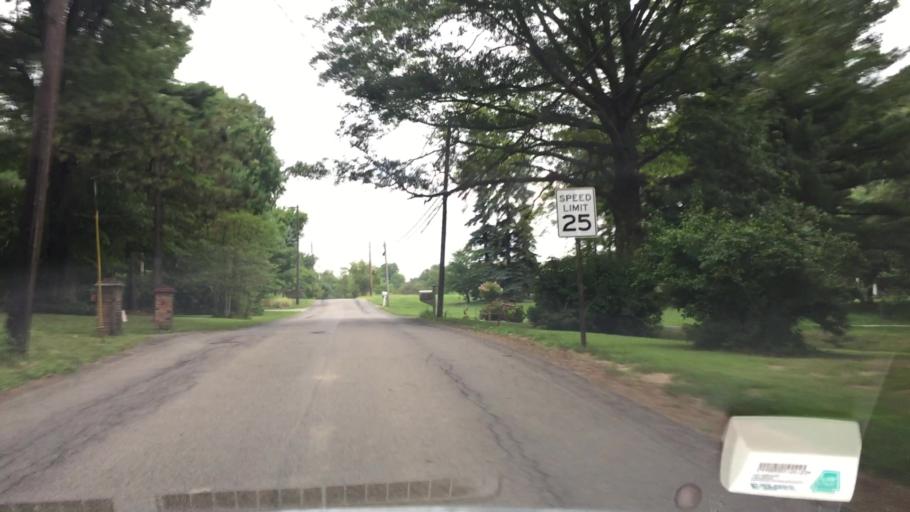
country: US
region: Pennsylvania
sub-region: Allegheny County
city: Allison Park
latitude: 40.5746
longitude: -79.9206
